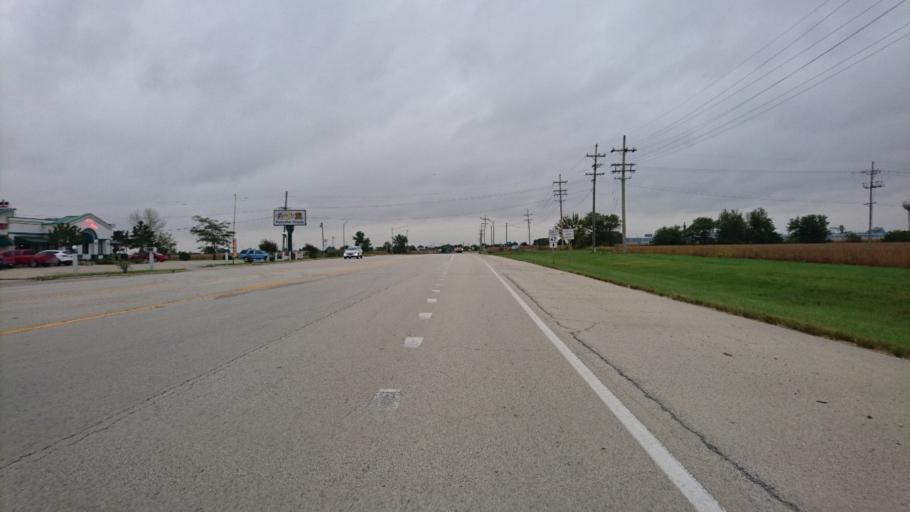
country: US
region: Illinois
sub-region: Livingston County
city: Dwight
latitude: 41.1113
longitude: -88.4138
